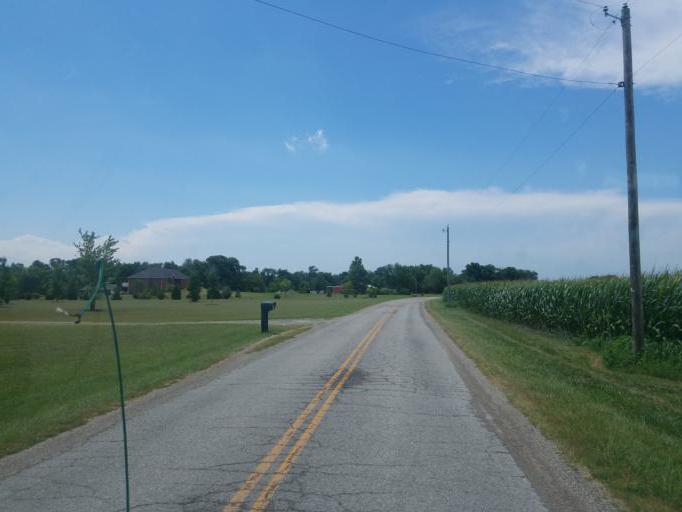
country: US
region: Ohio
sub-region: Paulding County
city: Antwerp
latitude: 41.1968
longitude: -84.7347
